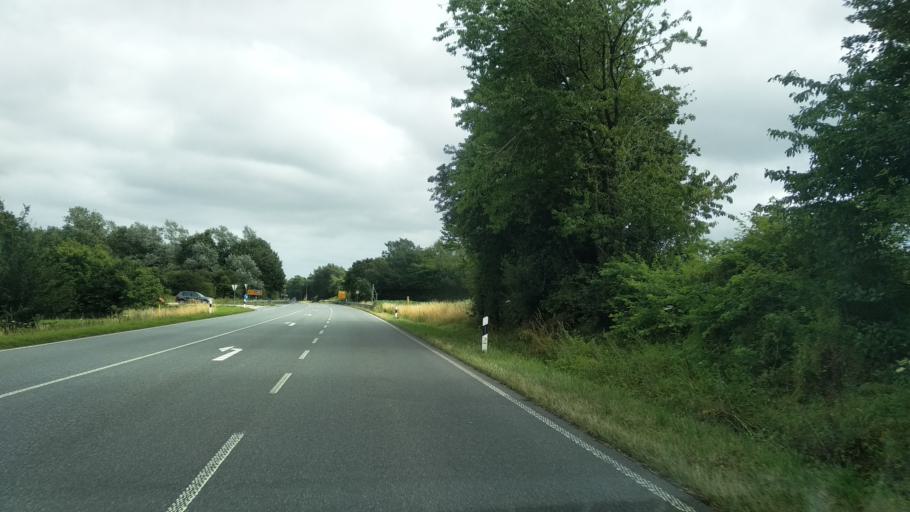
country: DE
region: Schleswig-Holstein
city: Schleswig
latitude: 54.5372
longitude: 9.5549
